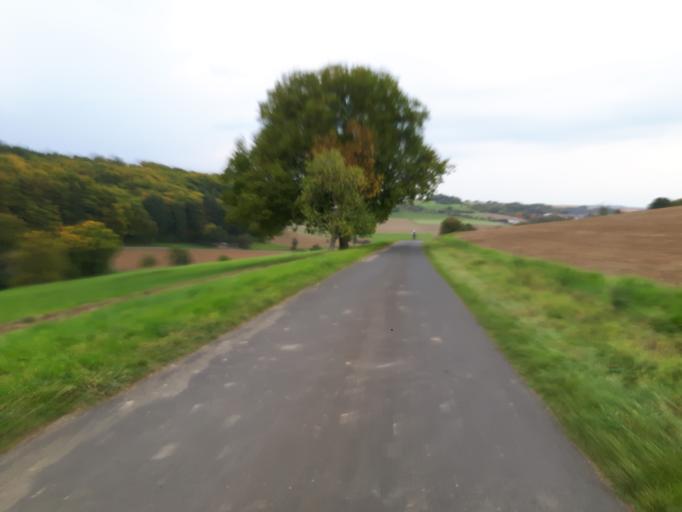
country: DE
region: Baden-Wuerttemberg
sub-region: Regierungsbezirk Stuttgart
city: Assamstadt
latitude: 49.4350
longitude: 9.7449
